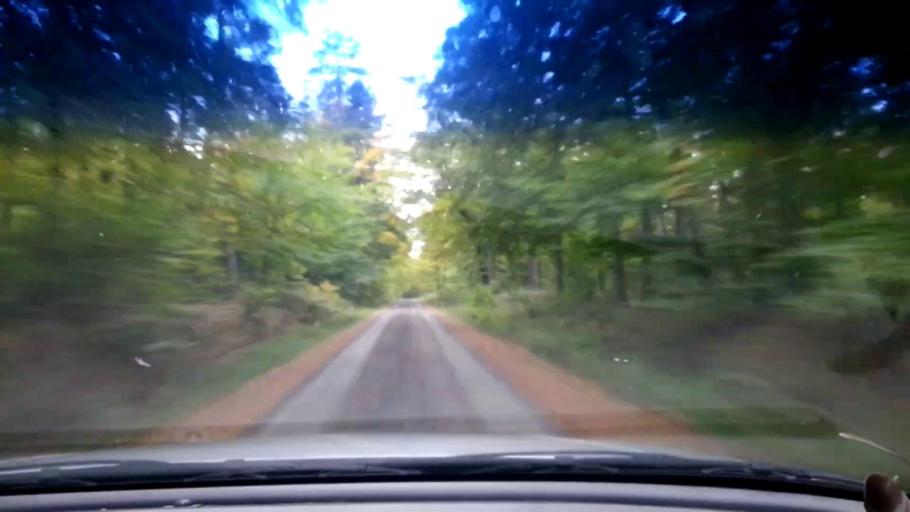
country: DE
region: Bavaria
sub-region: Upper Franconia
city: Burgwindheim
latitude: 49.8555
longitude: 10.6451
